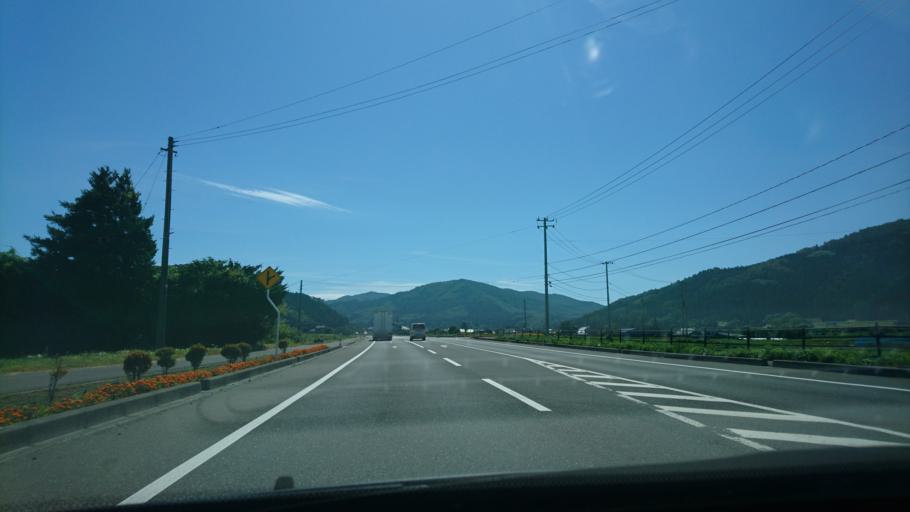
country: JP
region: Iwate
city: Tono
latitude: 39.2745
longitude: 141.5790
